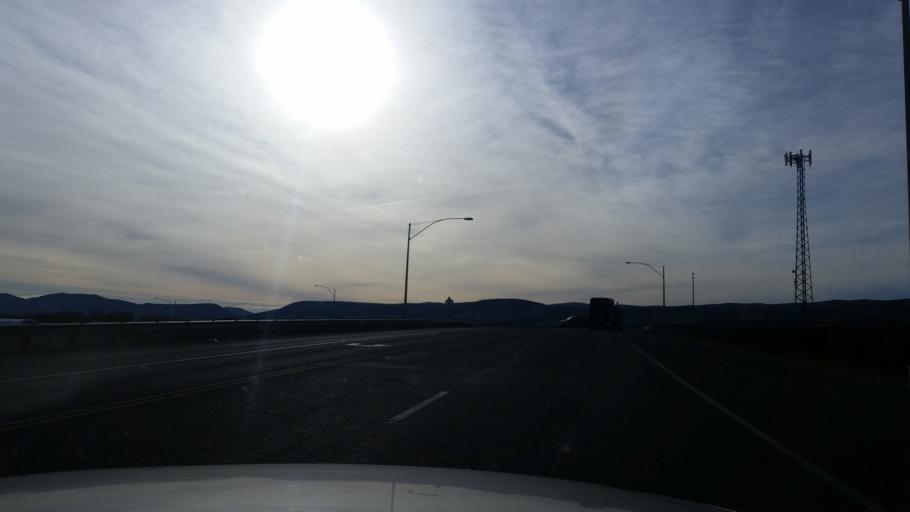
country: US
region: Washington
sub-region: Kittitas County
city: Ellensburg
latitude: 47.0119
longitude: -120.5751
